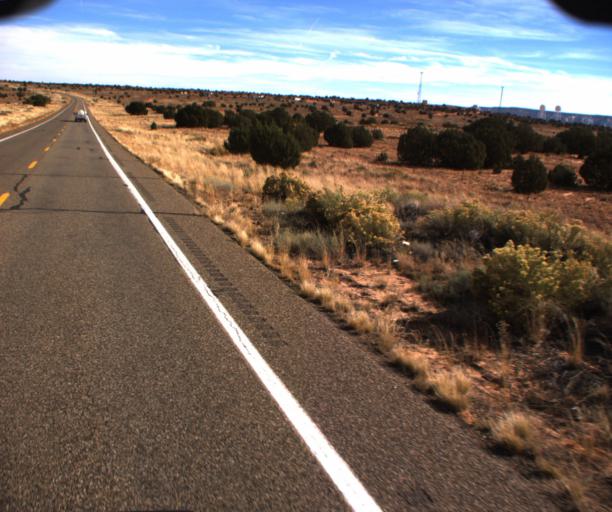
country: US
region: Arizona
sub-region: Coconino County
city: Kaibito
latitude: 36.5792
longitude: -111.1130
